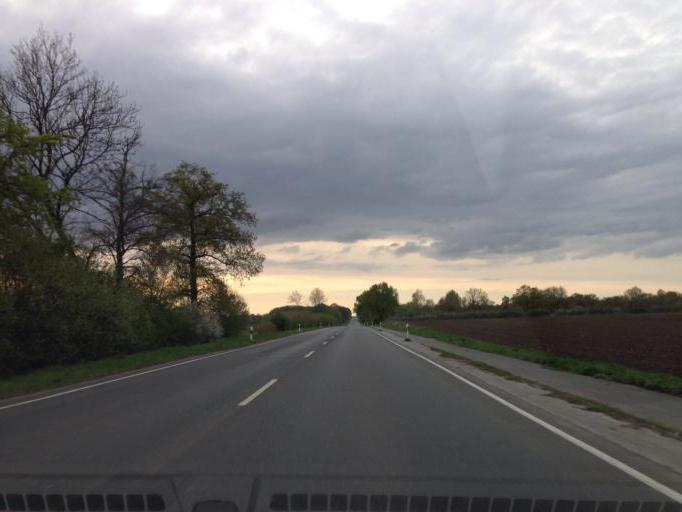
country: DE
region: North Rhine-Westphalia
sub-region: Regierungsbezirk Munster
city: Altenberge
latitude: 52.0240
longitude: 7.4948
